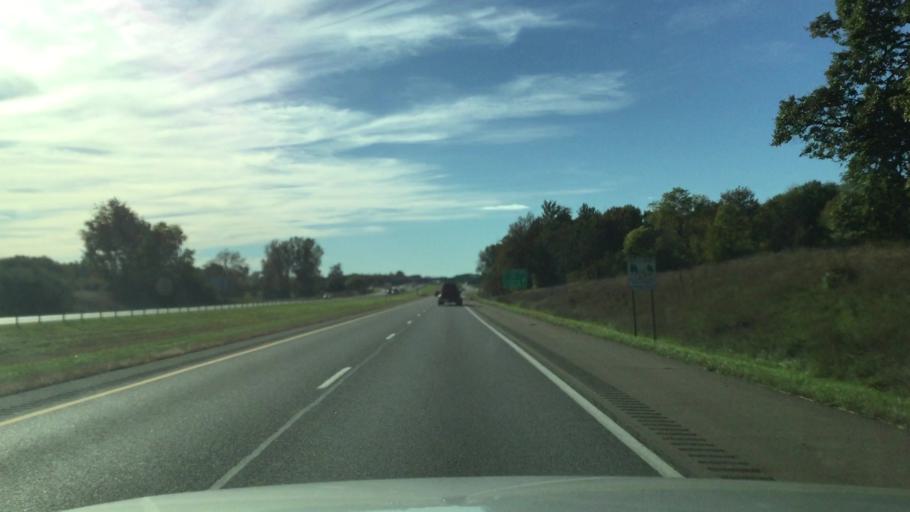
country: US
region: Michigan
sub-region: Calhoun County
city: Marshall
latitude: 42.2974
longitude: -84.9816
